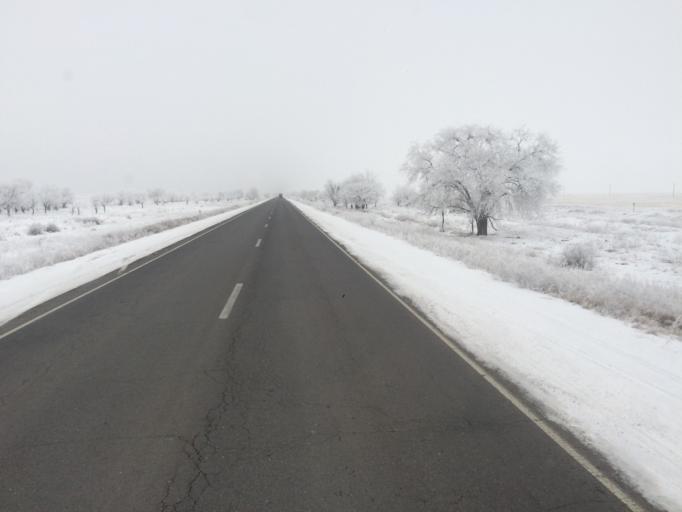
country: KG
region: Chuy
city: Tokmok
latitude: 43.3659
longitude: 75.3388
